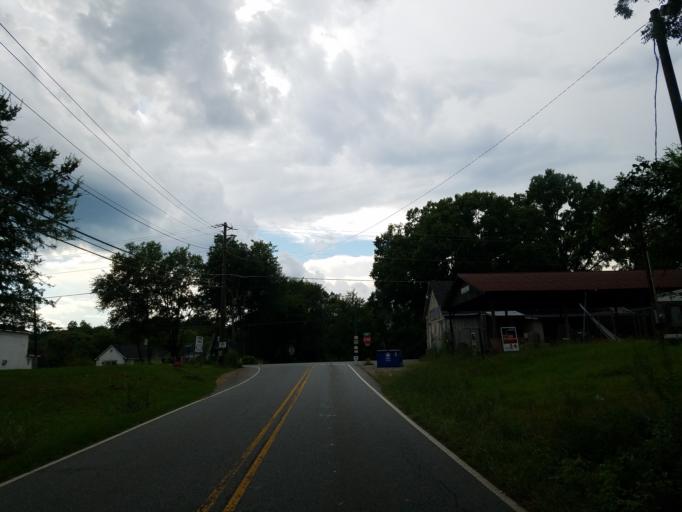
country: US
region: Georgia
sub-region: Bartow County
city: Cartersville
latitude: 34.2494
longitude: -84.8518
